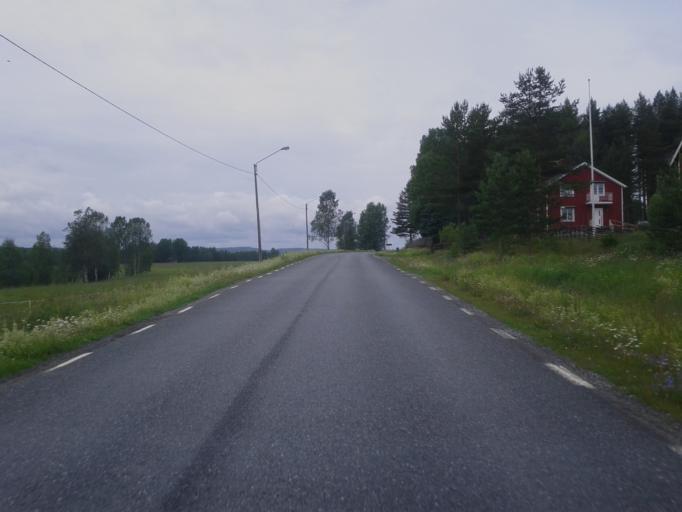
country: SE
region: Vaesterbotten
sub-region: Skelleftea Kommun
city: Forsbacka
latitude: 64.9046
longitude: 20.6447
